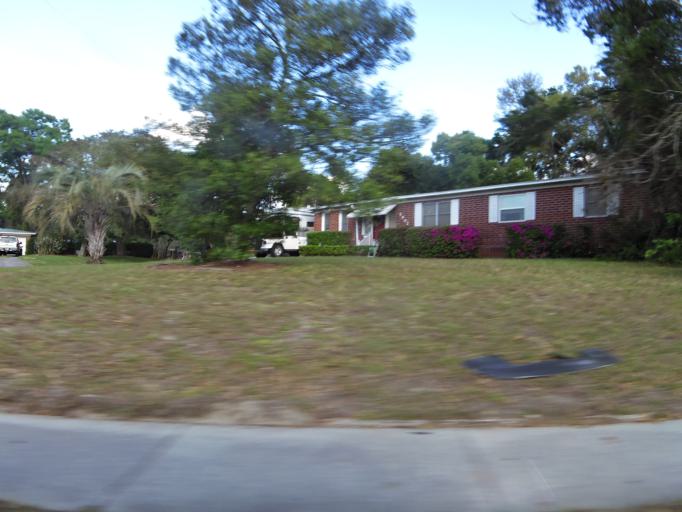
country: US
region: Florida
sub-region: Duval County
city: Jacksonville
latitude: 30.3448
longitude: -81.5976
